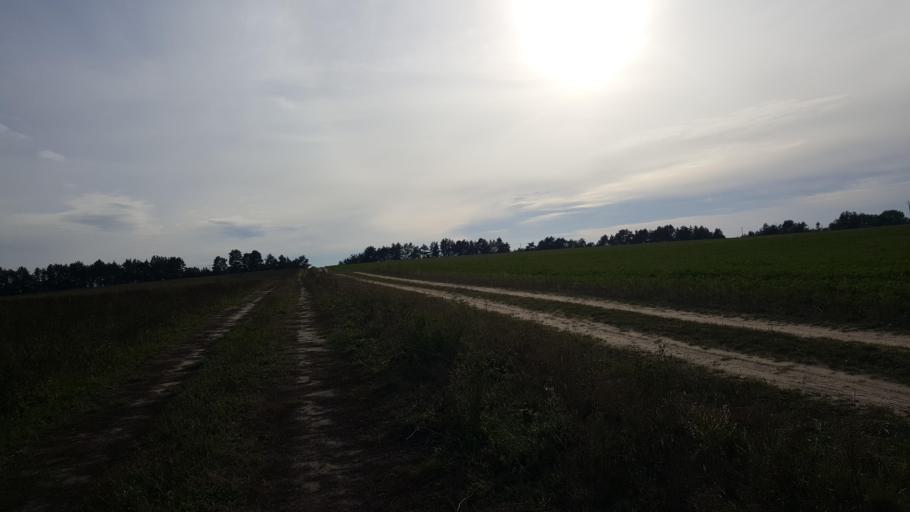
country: BY
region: Brest
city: Kamyanyets
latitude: 52.4016
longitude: 23.8580
